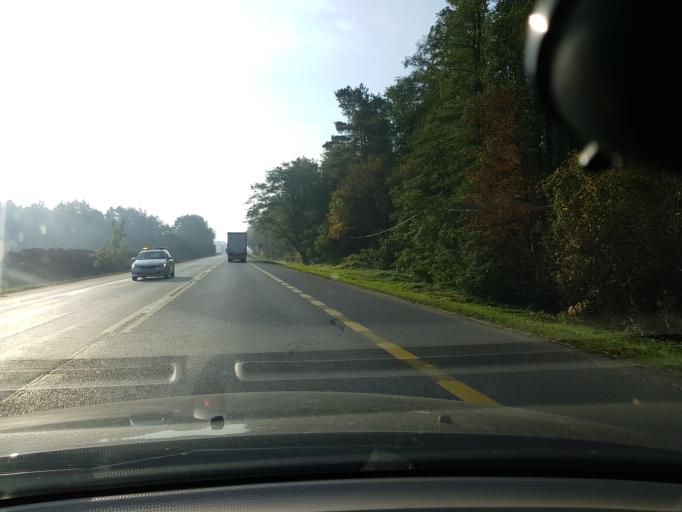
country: PL
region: Masovian Voivodeship
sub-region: Powiat otwocki
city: Otwock
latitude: 52.1487
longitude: 21.3197
